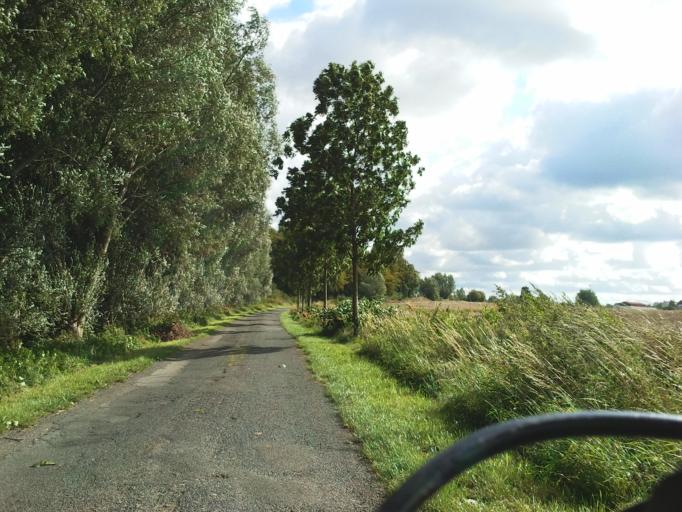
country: DE
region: Mecklenburg-Vorpommern
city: Dierkow-West
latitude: 54.1122
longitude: 12.1214
